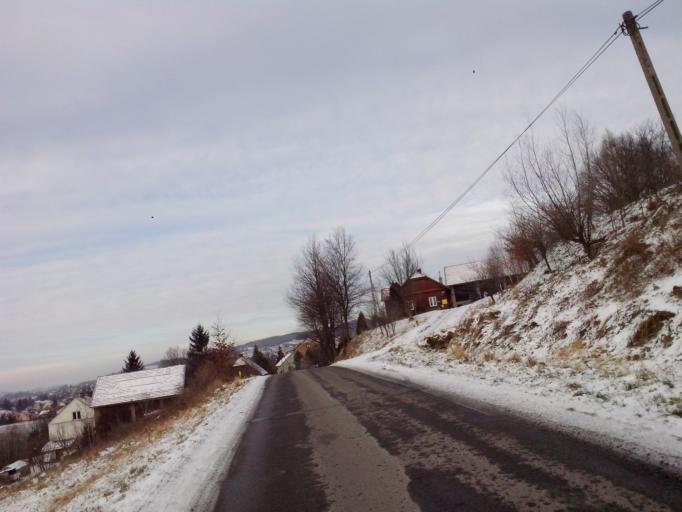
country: PL
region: Subcarpathian Voivodeship
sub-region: Powiat strzyzowski
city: Strzyzow
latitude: 49.8564
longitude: 21.8011
